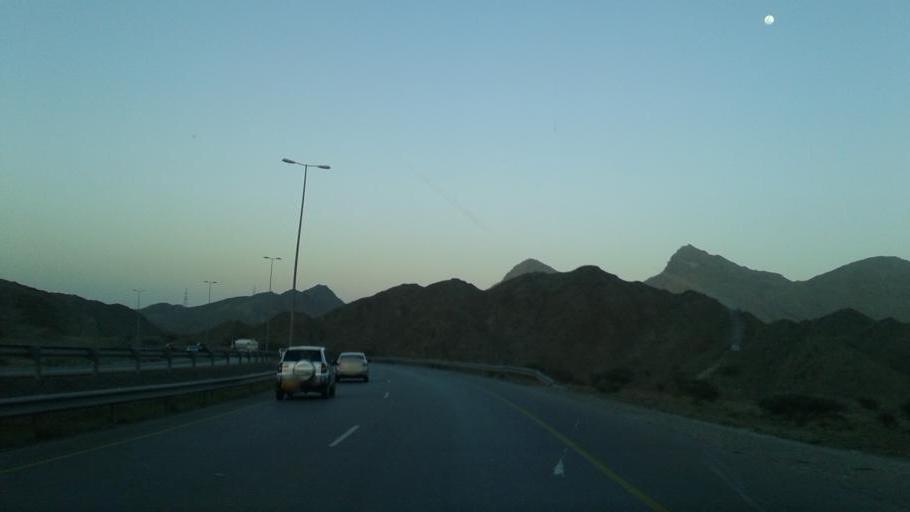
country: OM
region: Muhafazat ad Dakhiliyah
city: Bidbid
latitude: 23.4603
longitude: 58.1849
